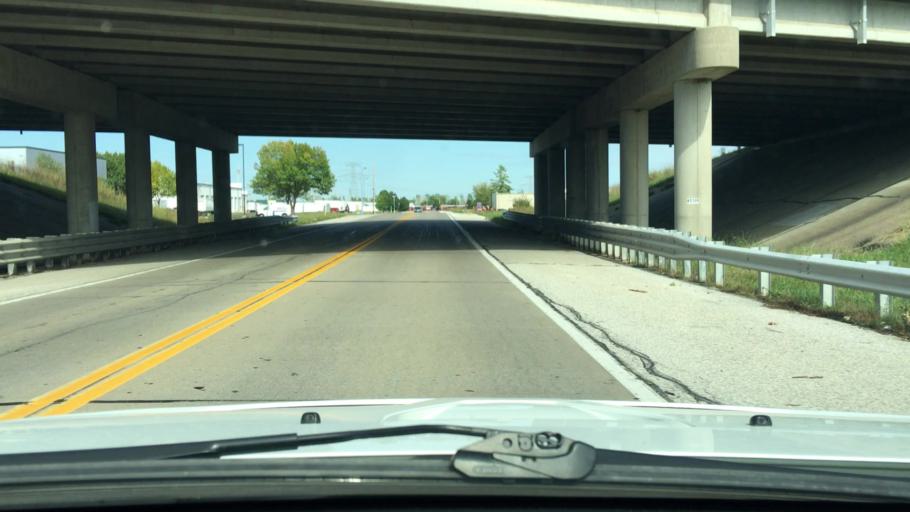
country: US
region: Missouri
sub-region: Saint Charles County
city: Saint Charles
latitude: 38.8208
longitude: -90.5068
